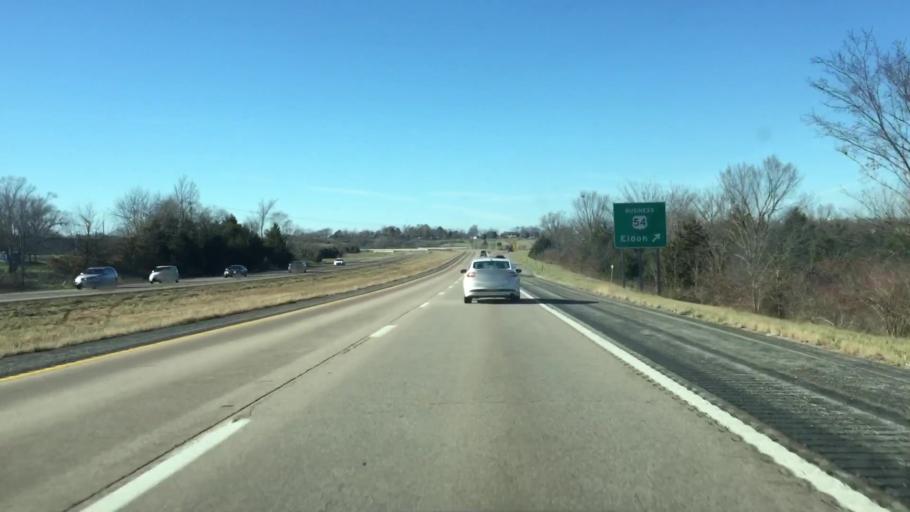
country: US
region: Missouri
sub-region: Miller County
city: Eldon
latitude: 38.3657
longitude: -92.5391
